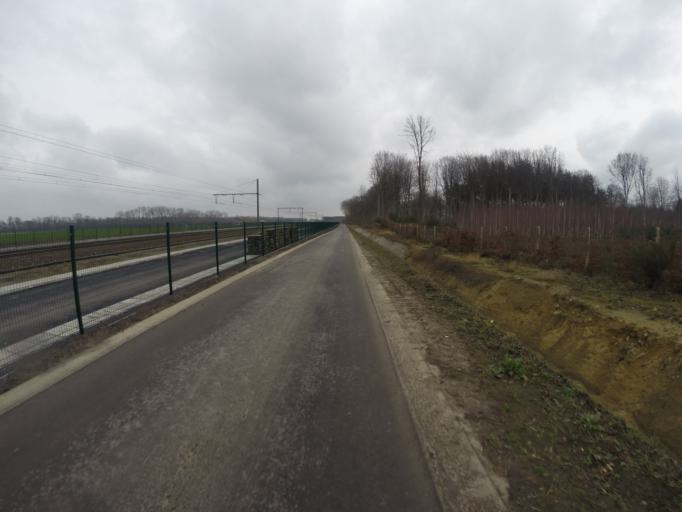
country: BE
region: Flanders
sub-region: Provincie Oost-Vlaanderen
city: Knesselare
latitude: 51.1062
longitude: 3.3900
